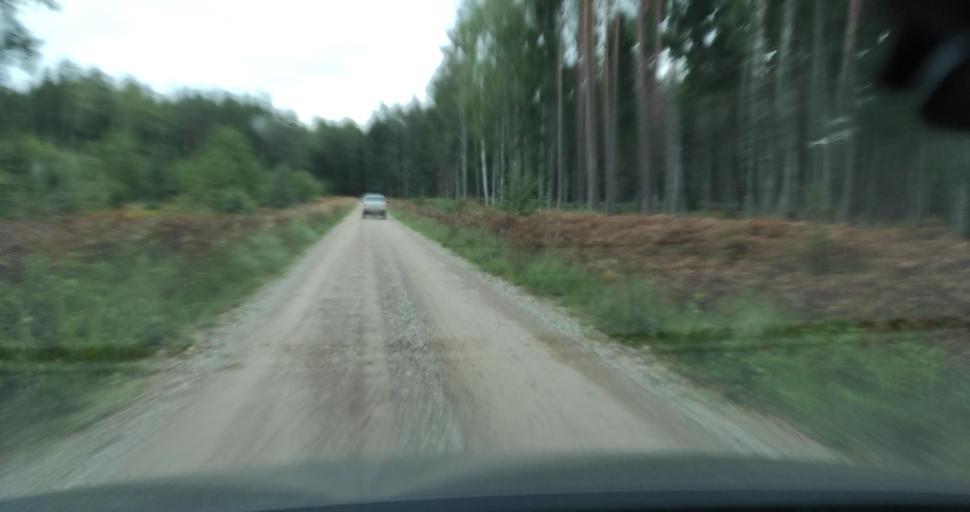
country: LV
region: Talsu Rajons
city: Stende
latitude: 57.0299
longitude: 22.3319
